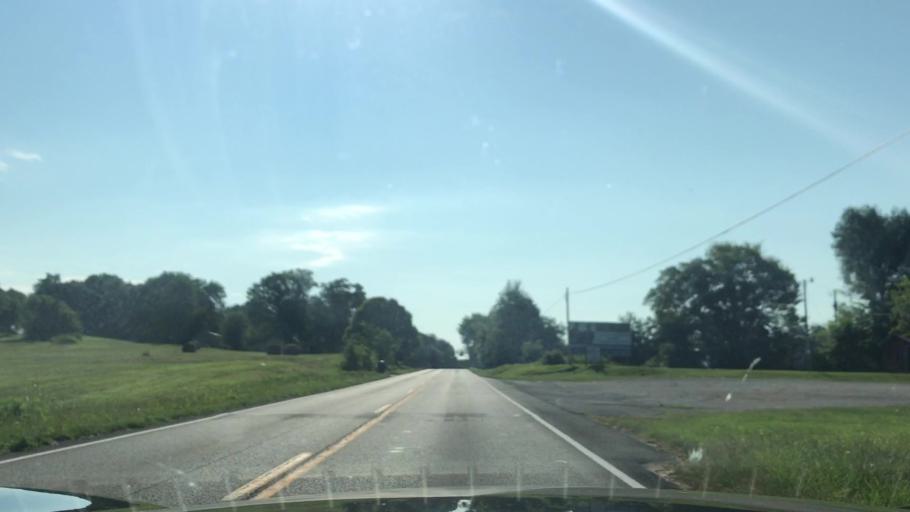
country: US
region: Kentucky
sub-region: Hart County
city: Horse Cave
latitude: 37.1763
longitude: -85.8716
